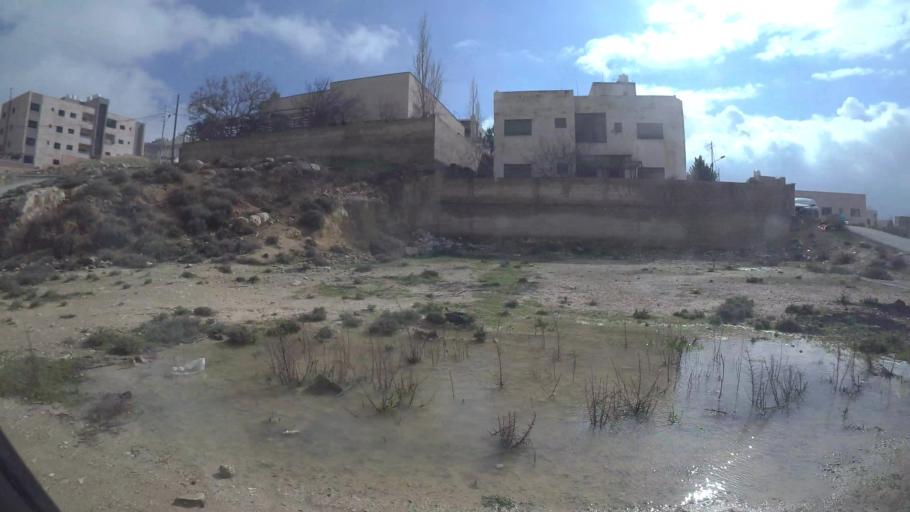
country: JO
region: Amman
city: Al Jubayhah
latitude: 32.0619
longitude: 35.8626
